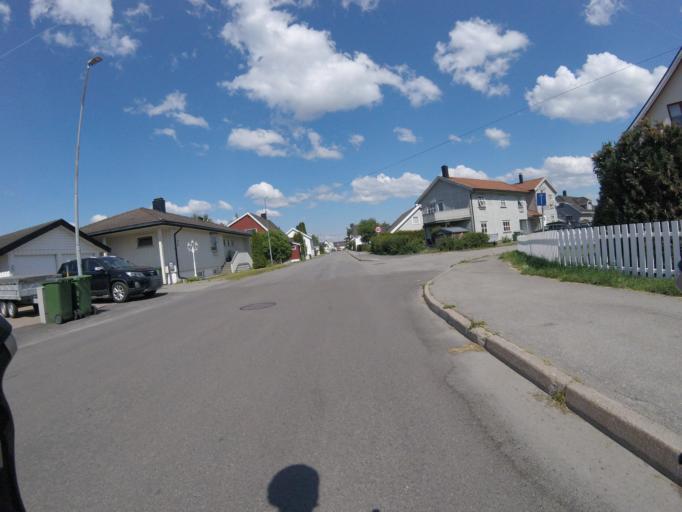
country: NO
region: Akershus
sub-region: Skedsmo
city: Lillestrom
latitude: 59.9493
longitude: 11.0614
